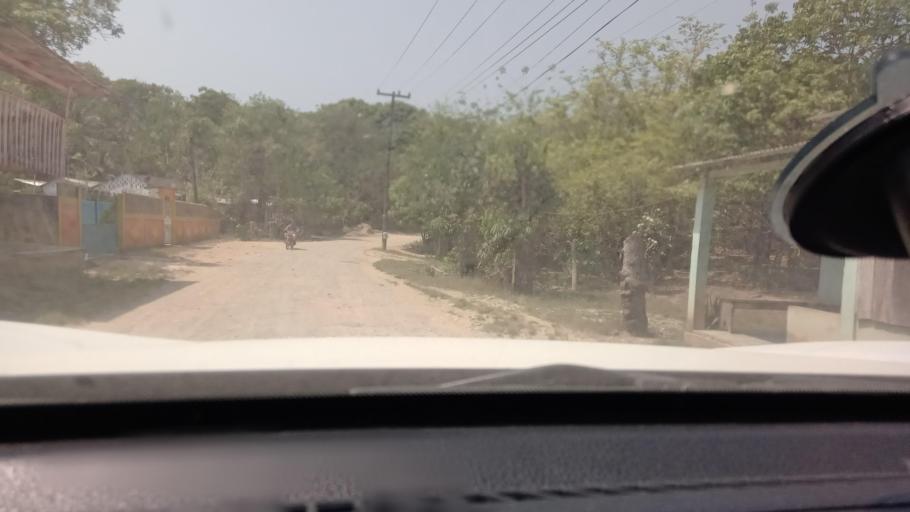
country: MX
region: Tabasco
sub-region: Huimanguillo
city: Francisco Rueda
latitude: 17.5009
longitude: -93.9043
